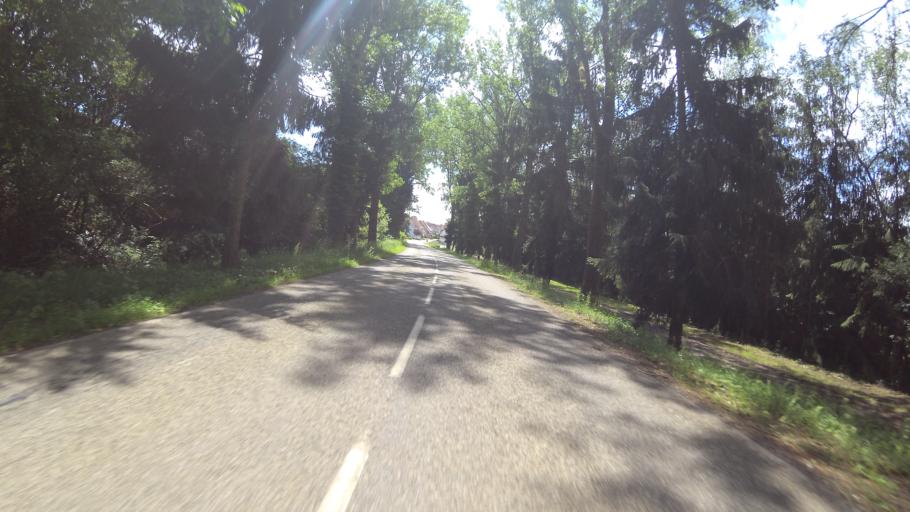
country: FR
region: Alsace
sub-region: Departement du Bas-Rhin
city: Oermingen
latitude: 48.9662
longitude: 7.1379
